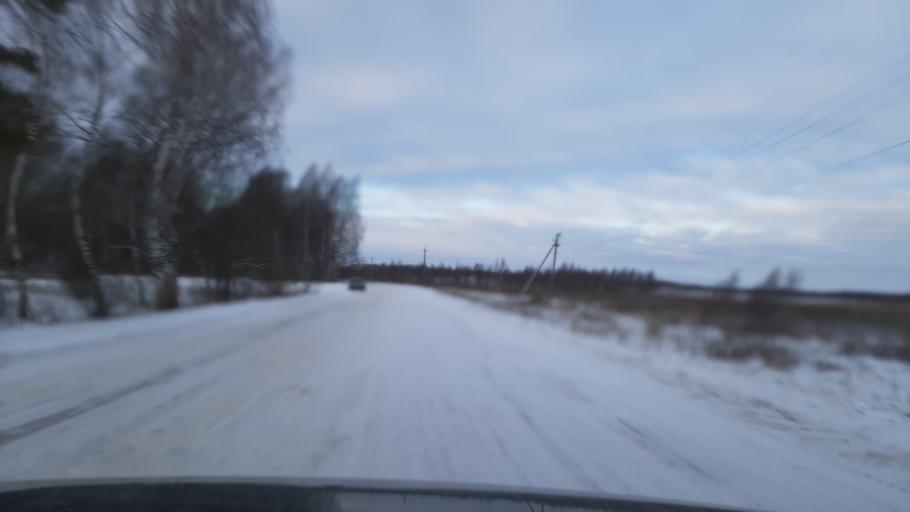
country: RU
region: Kostroma
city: Nerekhta
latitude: 57.4715
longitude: 40.6717
